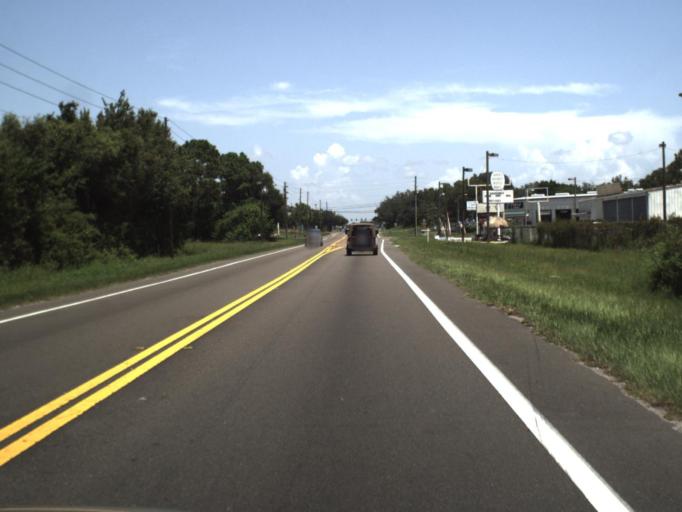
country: US
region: Florida
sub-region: Pinellas County
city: Tarpon Springs
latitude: 28.1690
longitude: -82.7543
